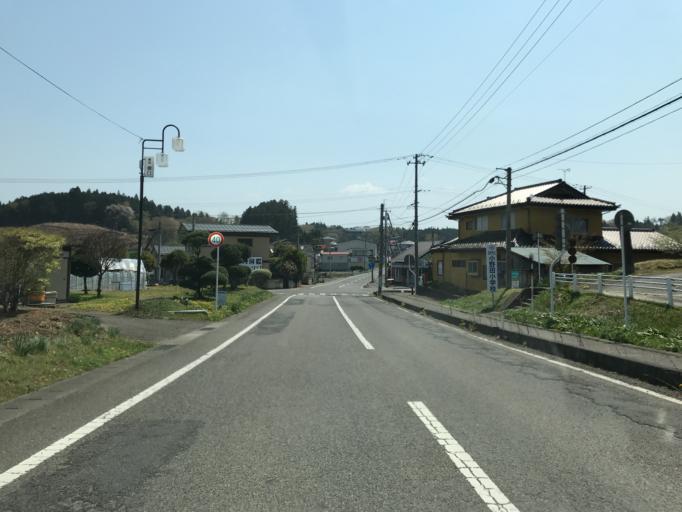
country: JP
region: Fukushima
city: Ishikawa
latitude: 37.1098
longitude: 140.3855
